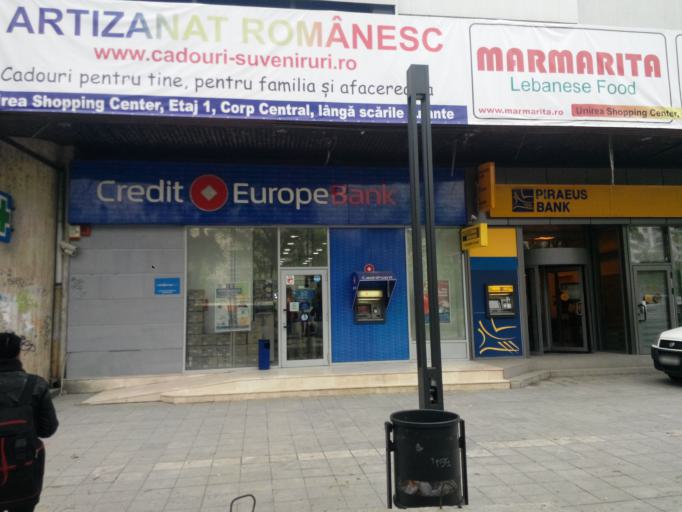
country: RO
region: Bucuresti
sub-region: Municipiul Bucuresti
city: Bucharest
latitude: 44.4271
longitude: 26.1050
